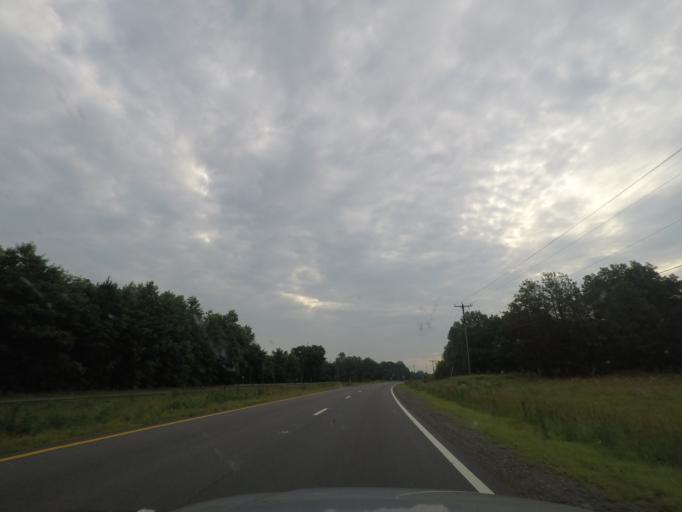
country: US
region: Virginia
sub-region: Halifax County
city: Halifax
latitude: 36.8138
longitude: -78.7496
